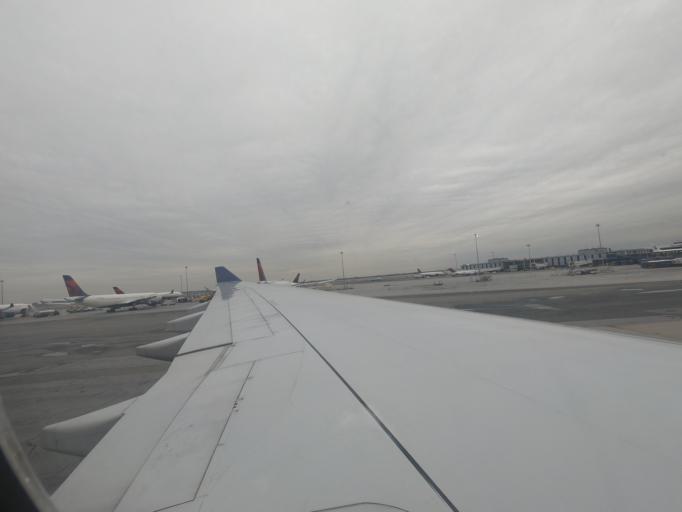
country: US
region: New York
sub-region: Nassau County
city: Inwood
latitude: 40.6409
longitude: -73.7844
